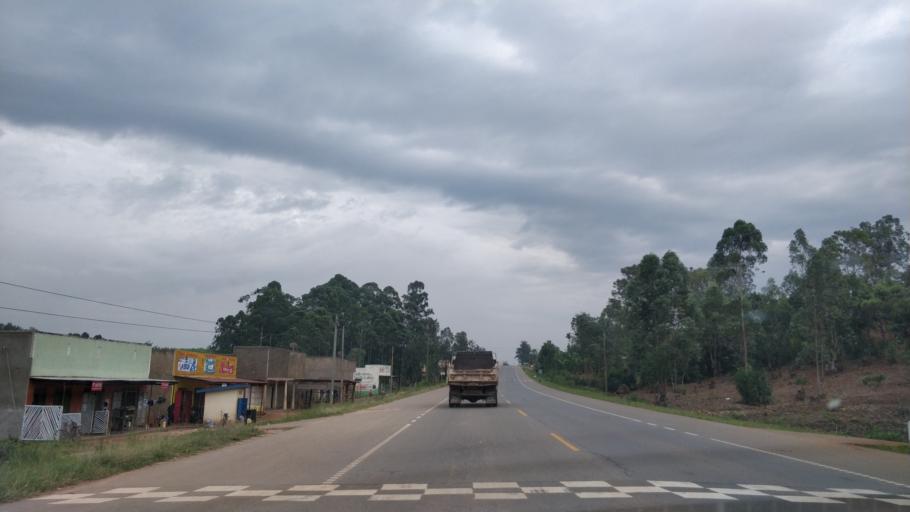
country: UG
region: Western Region
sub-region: Sheema District
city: Kibingo
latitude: -0.6591
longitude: 30.4610
